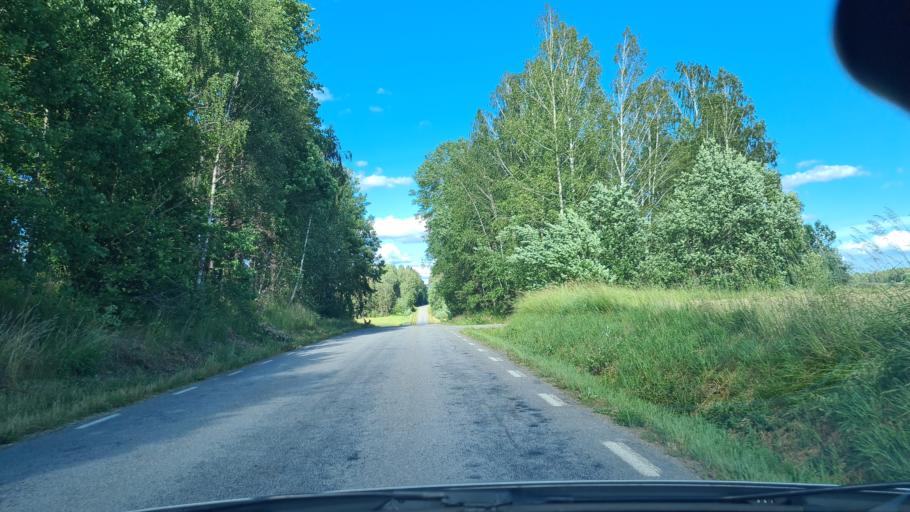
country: SE
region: Soedermanland
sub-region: Nykopings Kommun
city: Olstorp
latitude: 58.8193
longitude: 16.4898
